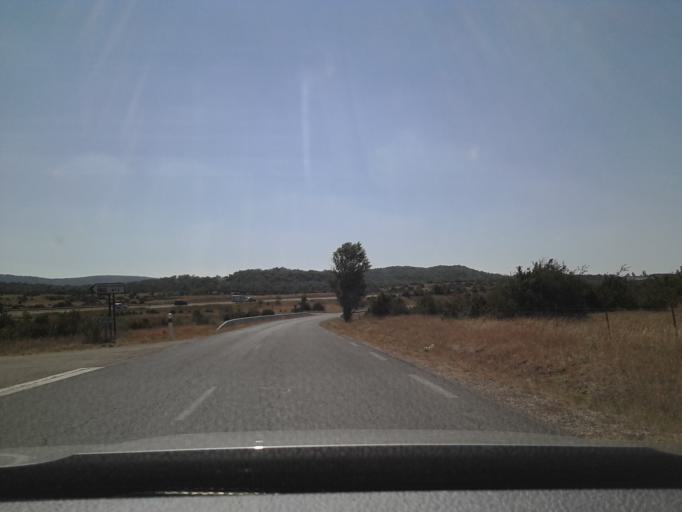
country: FR
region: Midi-Pyrenees
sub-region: Departement de l'Aveyron
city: La Cavalerie
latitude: 43.9332
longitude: 3.2296
